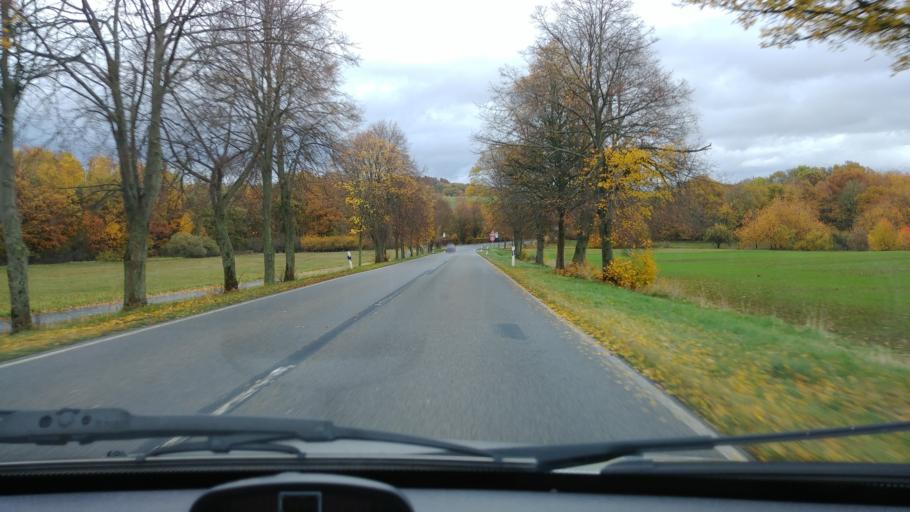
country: DE
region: Hesse
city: Mengerskirchen
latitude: 50.5431
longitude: 8.1476
